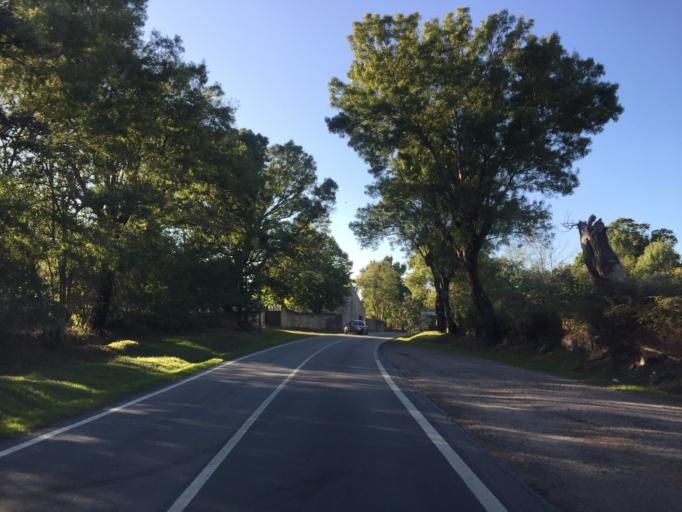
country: PT
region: Portalegre
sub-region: Castelo de Vide
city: Castelo de Vide
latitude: 39.3964
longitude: -7.4244
